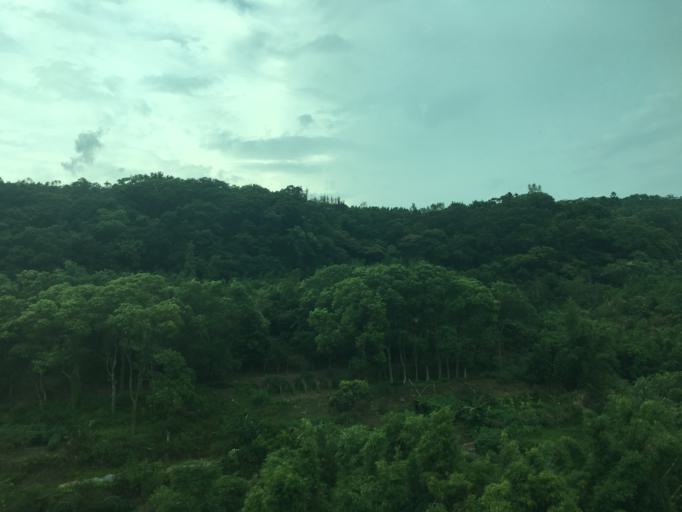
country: TW
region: Taiwan
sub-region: Taoyuan
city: Taoyuan
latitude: 25.0651
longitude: 121.3326
